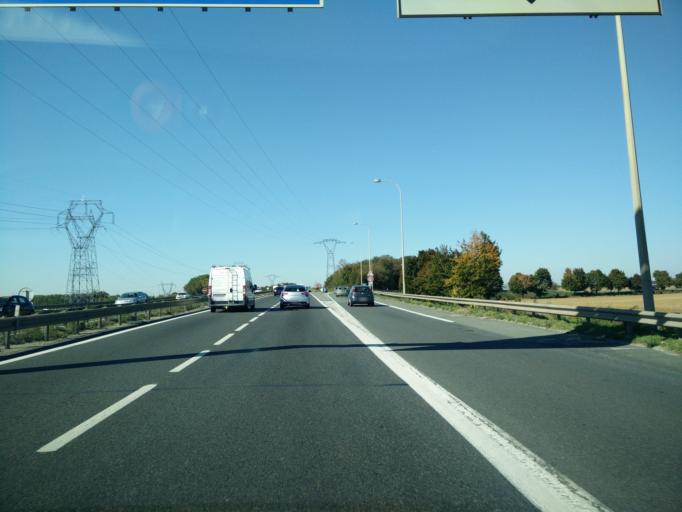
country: FR
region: Ile-de-France
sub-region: Departement de Seine-et-Marne
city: Mitry-Mory
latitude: 48.9744
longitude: 2.5883
